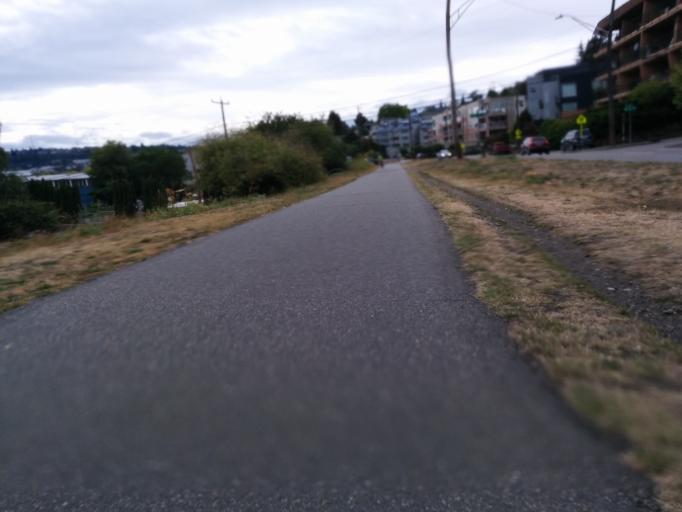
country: US
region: Washington
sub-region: King County
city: Seattle
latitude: 47.6551
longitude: -122.3240
